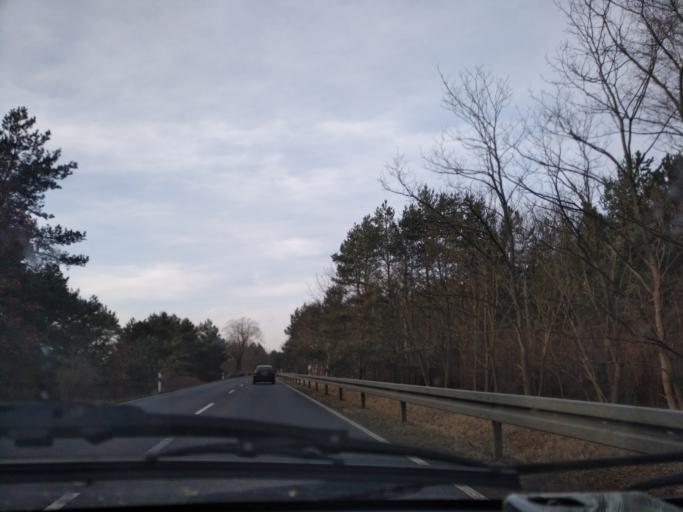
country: DE
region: Saxony-Anhalt
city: Holzdorf
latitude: 51.7677
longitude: 13.1997
